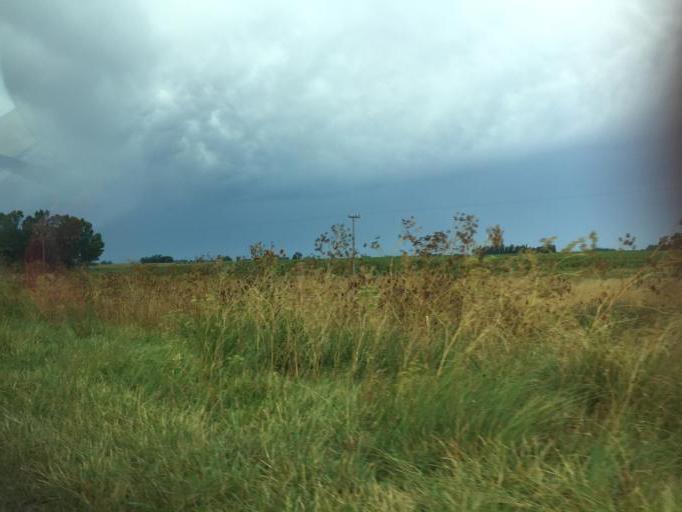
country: AR
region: Buenos Aires
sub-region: Partido de Rauch
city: Rauch
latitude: -36.9141
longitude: -58.9866
